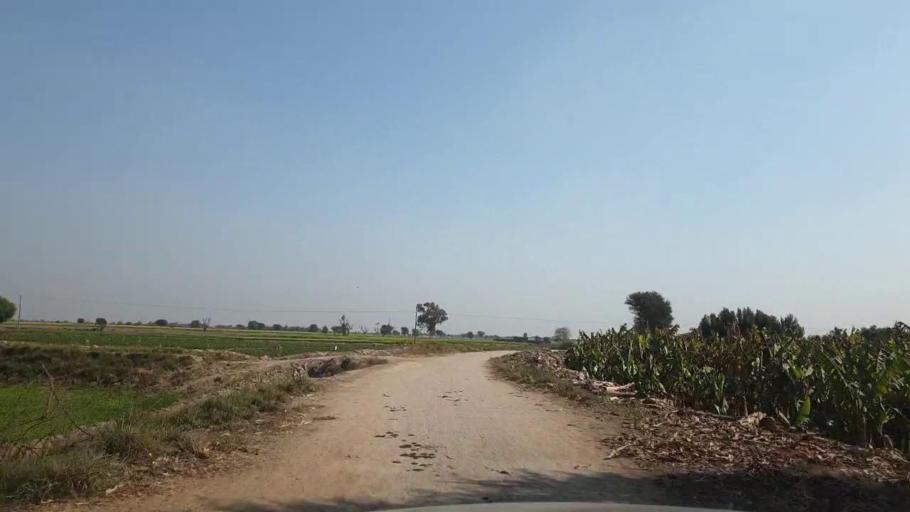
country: PK
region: Sindh
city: Tando Allahyar
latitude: 25.5863
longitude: 68.7513
